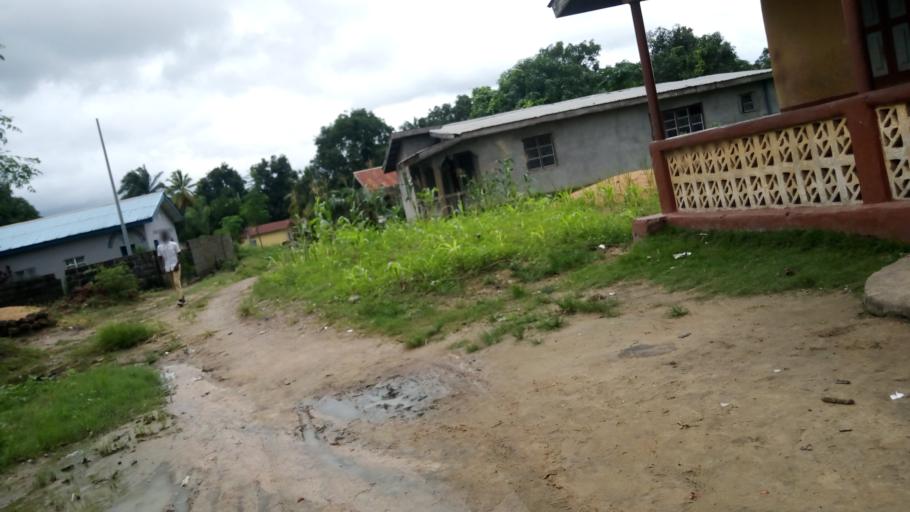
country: SL
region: Northern Province
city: Lunsar
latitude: 8.6901
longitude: -12.5346
